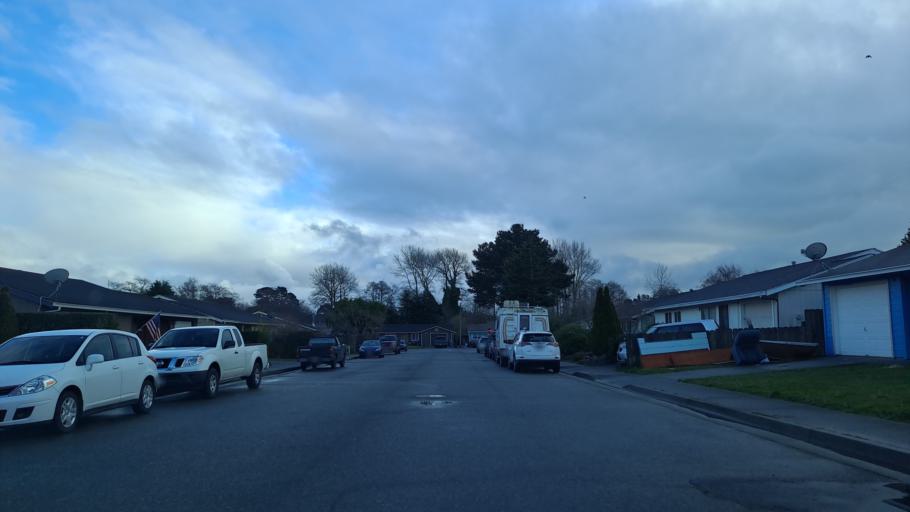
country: US
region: California
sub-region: Humboldt County
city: Fortuna
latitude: 40.5834
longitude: -124.1420
